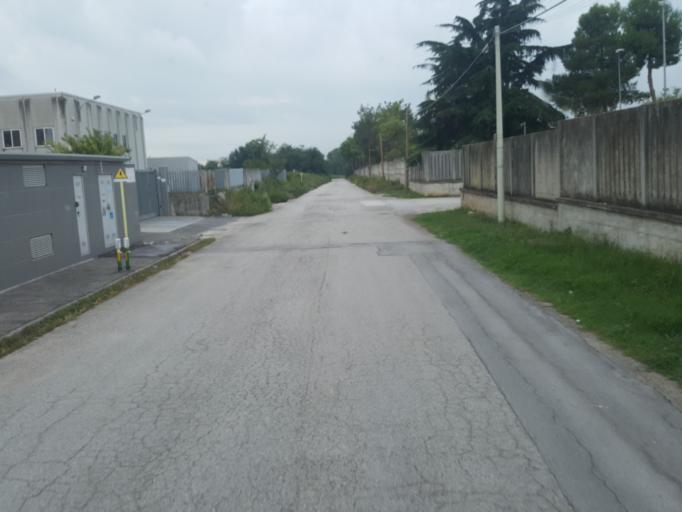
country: IT
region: Campania
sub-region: Provincia di Caserta
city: Pignataro Maggiore
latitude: 41.1702
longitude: 14.1552
